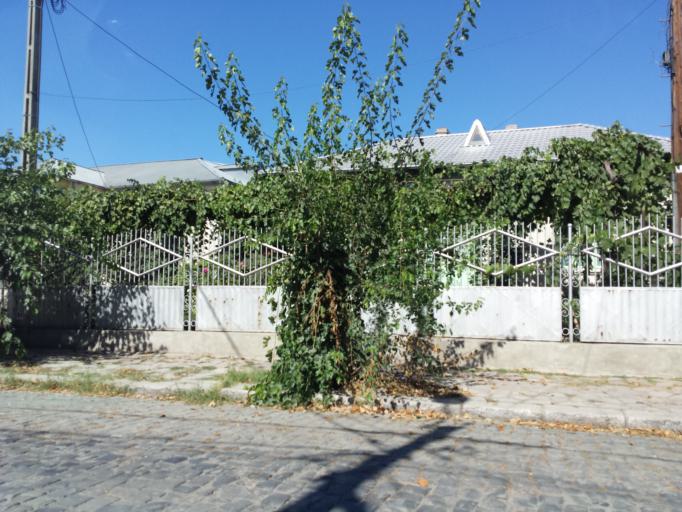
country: RO
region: Tulcea
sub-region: Municipiul Tulcea
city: Tulcea
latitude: 45.1849
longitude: 28.8128
